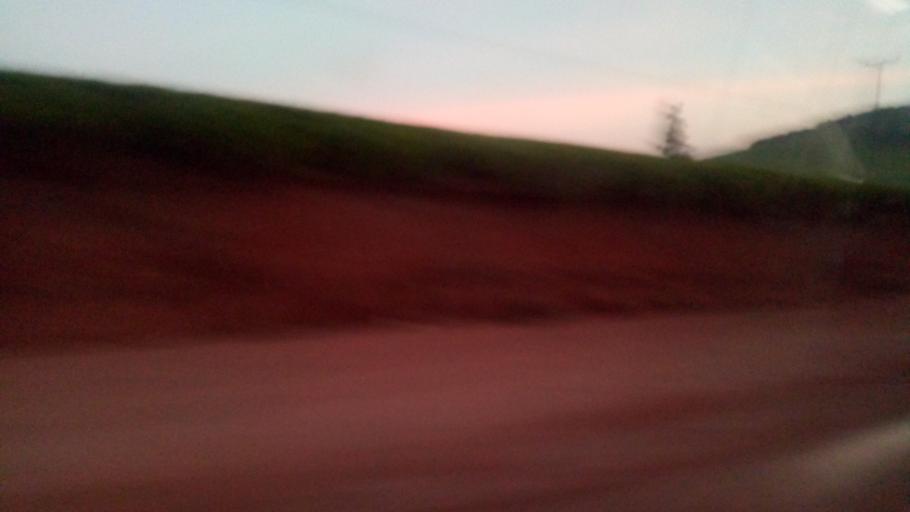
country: KE
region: Kericho
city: Sotik
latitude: -0.6181
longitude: 35.0581
